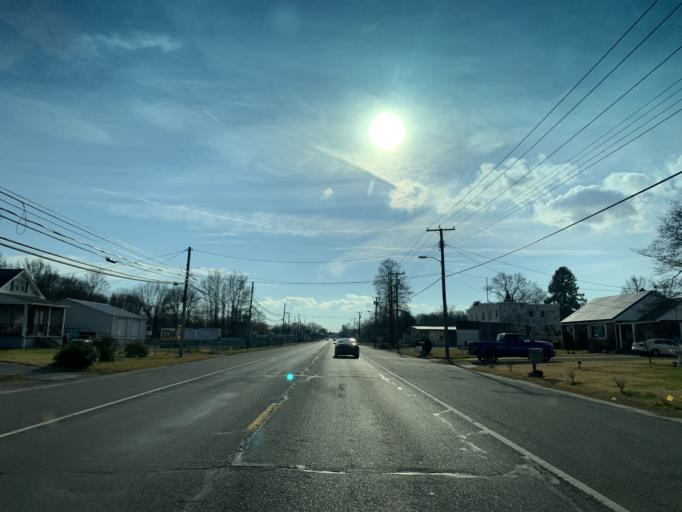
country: US
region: New Jersey
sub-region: Salem County
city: Penns Grove
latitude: 39.7388
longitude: -75.4571
